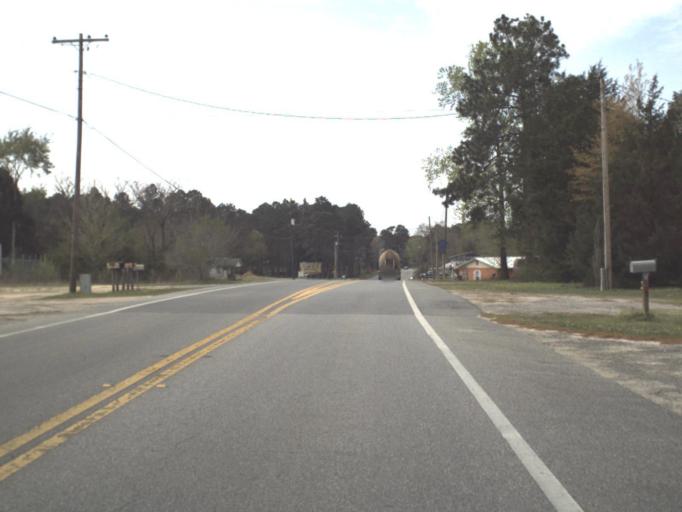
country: US
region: Florida
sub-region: Holmes County
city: Bonifay
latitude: 30.8232
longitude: -85.6690
